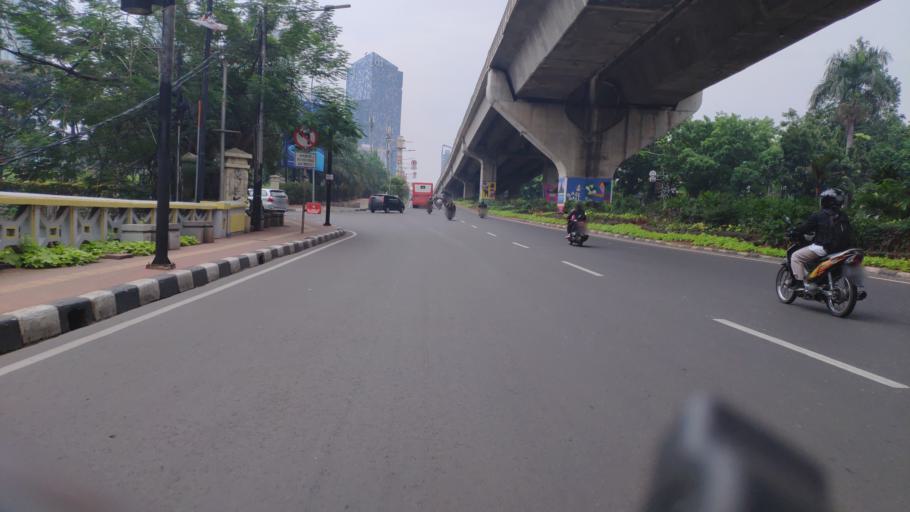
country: ID
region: Jakarta Raya
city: Jakarta
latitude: -6.2255
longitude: 106.8352
